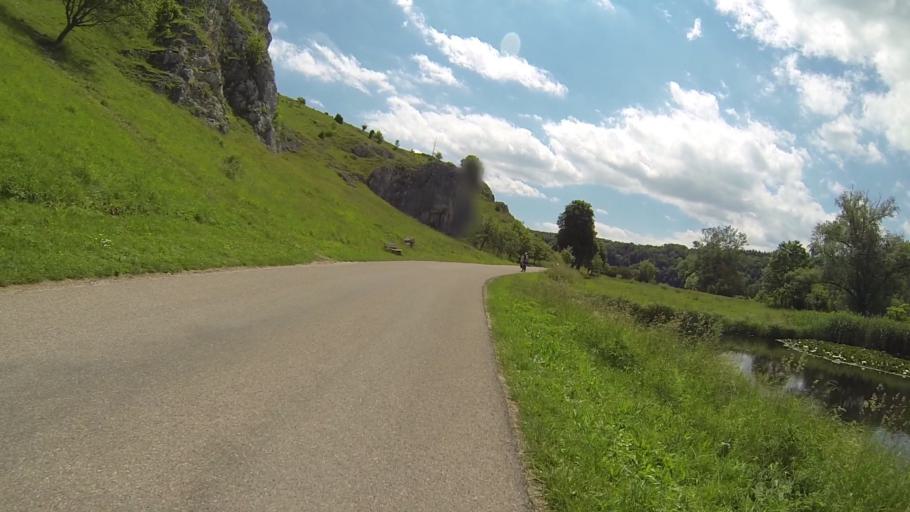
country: DE
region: Baden-Wuerttemberg
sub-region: Regierungsbezirk Stuttgart
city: Herbrechtingen
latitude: 48.6080
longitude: 10.1780
